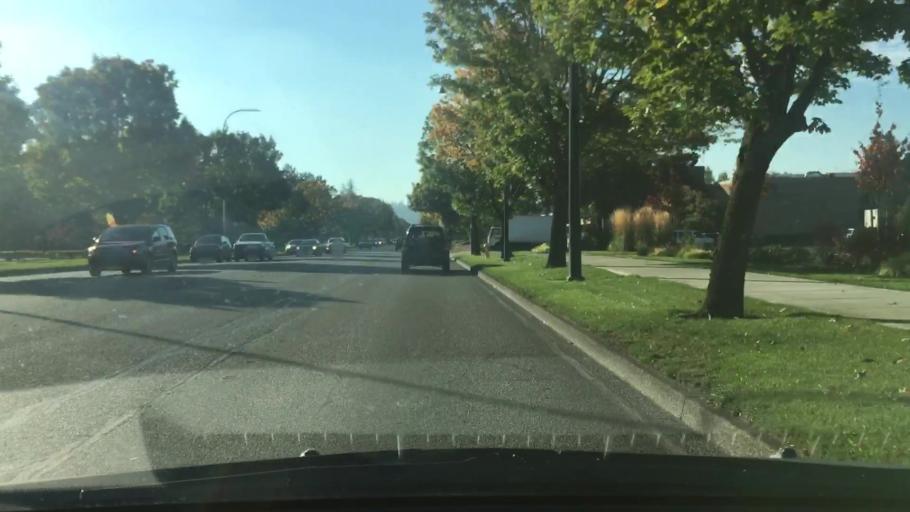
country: US
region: Washington
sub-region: King County
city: Renton
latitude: 47.4412
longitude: -122.2287
